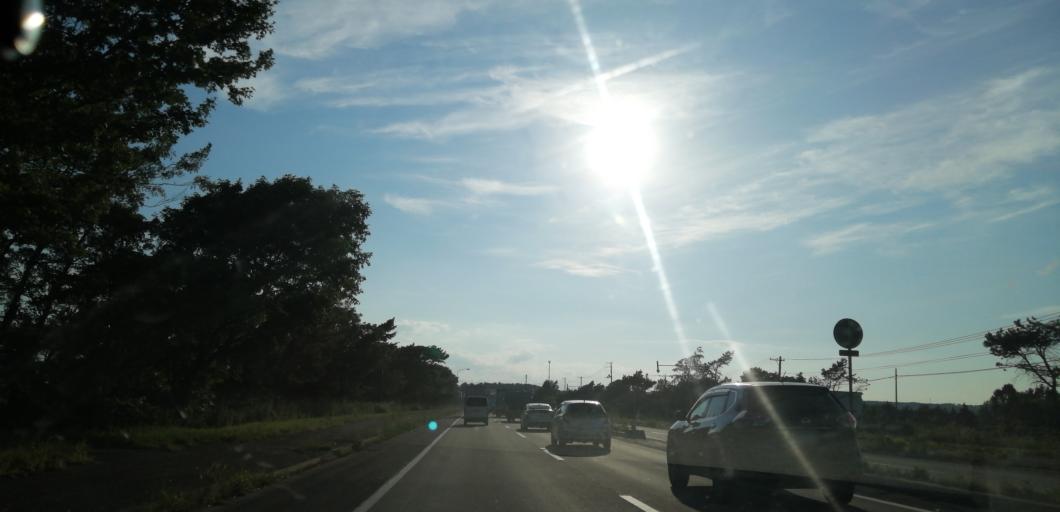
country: JP
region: Hokkaido
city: Kitahiroshima
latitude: 42.9973
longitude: 141.5752
